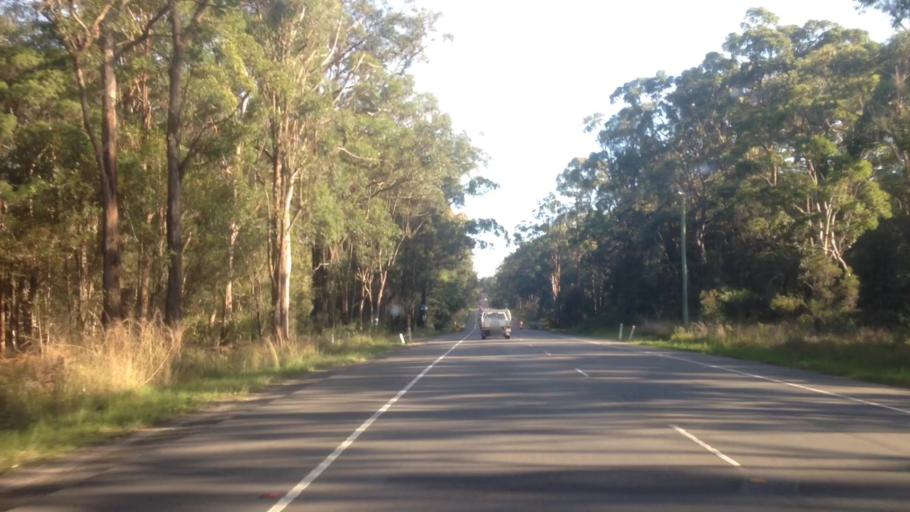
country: AU
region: New South Wales
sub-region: Lake Macquarie Shire
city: Dora Creek
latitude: -33.1346
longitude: 151.4771
